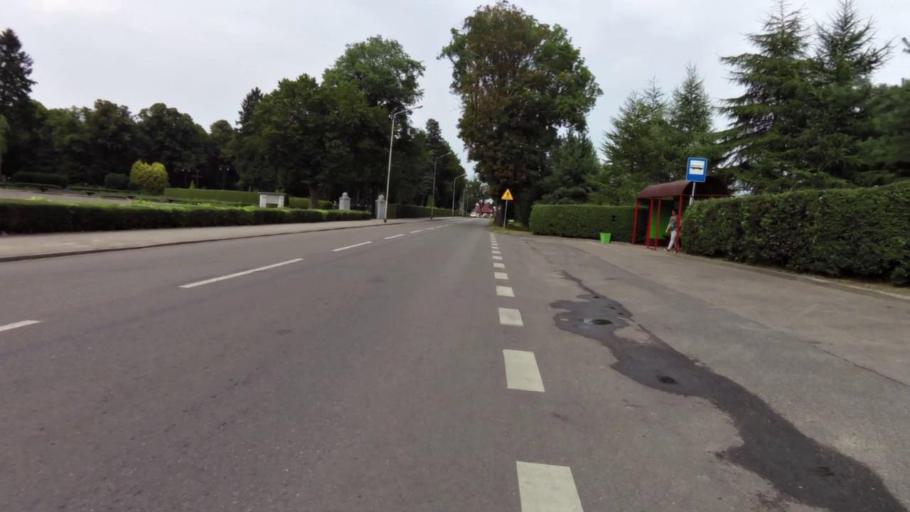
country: PL
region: West Pomeranian Voivodeship
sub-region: Powiat drawski
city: Drawsko Pomorskie
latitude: 53.5393
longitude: 15.8133
